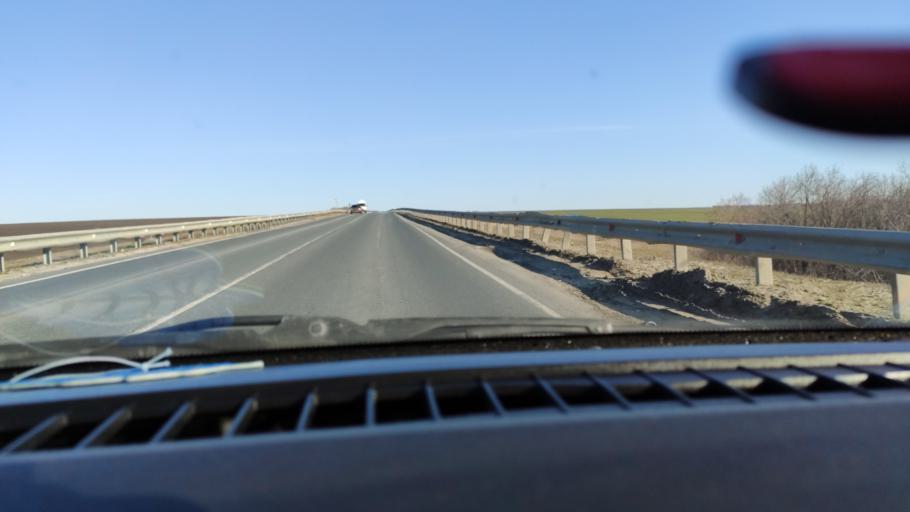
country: RU
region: Saratov
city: Dukhovnitskoye
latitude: 52.7525
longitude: 48.2473
